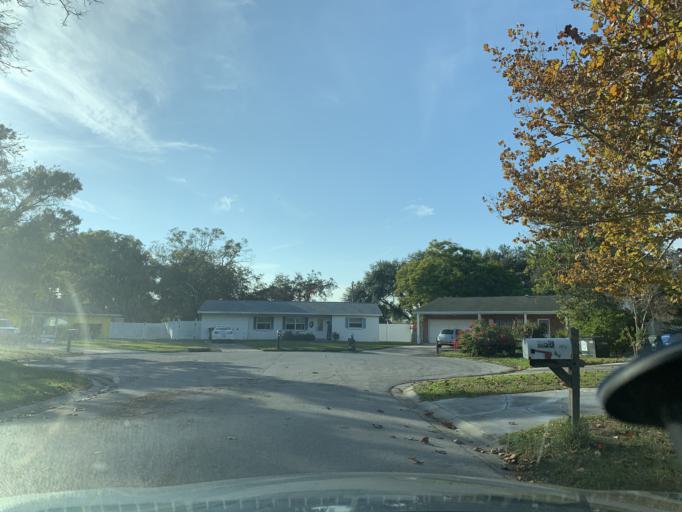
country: US
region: Florida
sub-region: Pinellas County
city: Ridgecrest
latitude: 27.8989
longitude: -82.7986
